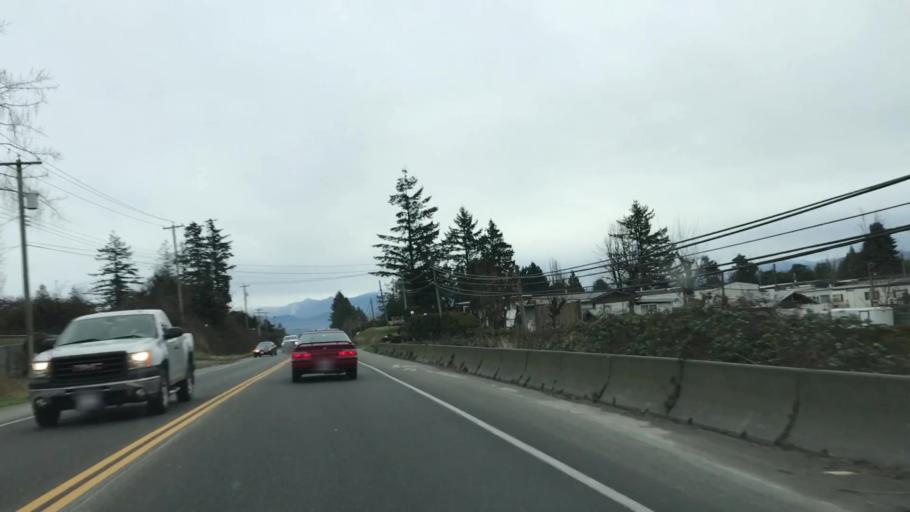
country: CA
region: British Columbia
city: Aldergrove
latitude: 49.0575
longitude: -122.4008
